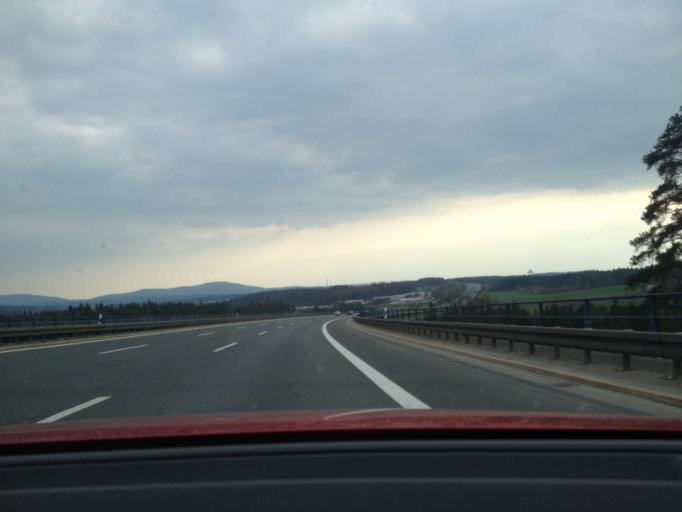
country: DE
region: Bavaria
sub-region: Regierungsbezirk Mittelfranken
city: Simmelsdorf
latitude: 49.5804
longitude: 11.3442
